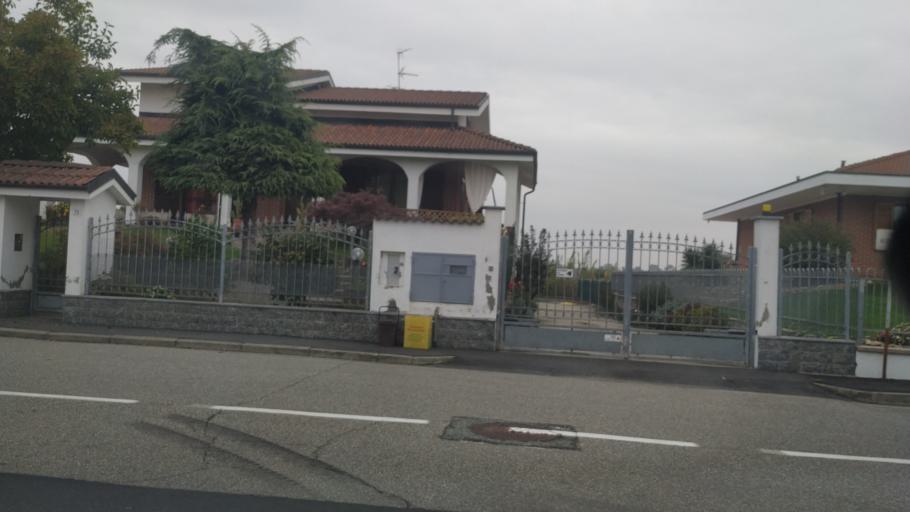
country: IT
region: Piedmont
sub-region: Provincia di Vercelli
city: Caresanablot
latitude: 45.3588
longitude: 8.3917
